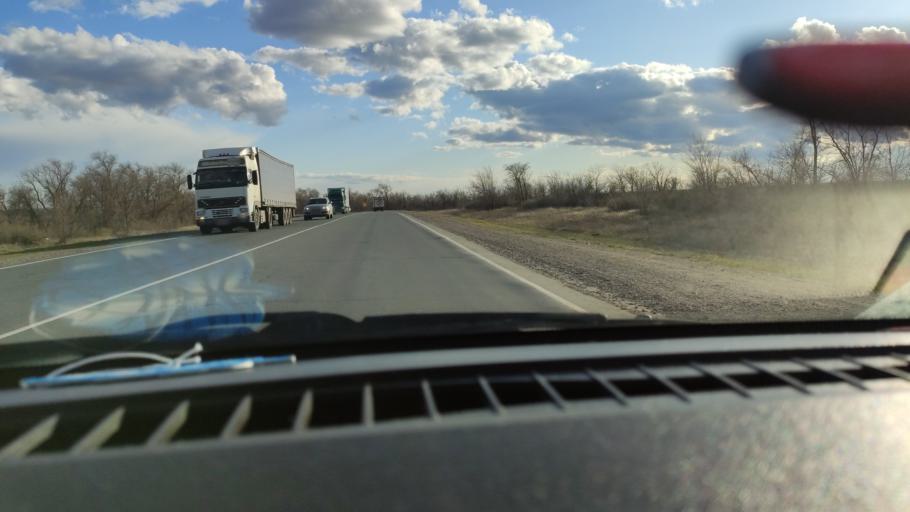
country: RU
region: Saratov
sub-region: Saratovskiy Rayon
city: Saratov
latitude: 51.7054
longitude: 46.0137
